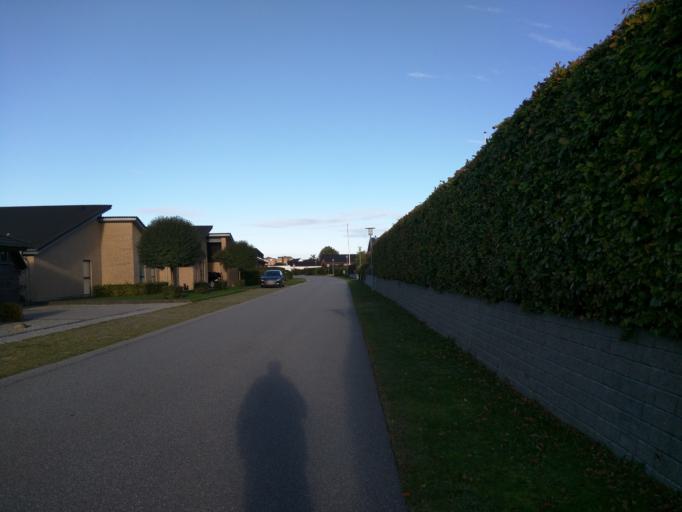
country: DK
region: Central Jutland
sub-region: Viborg Kommune
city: Viborg
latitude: 56.4375
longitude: 9.3716
